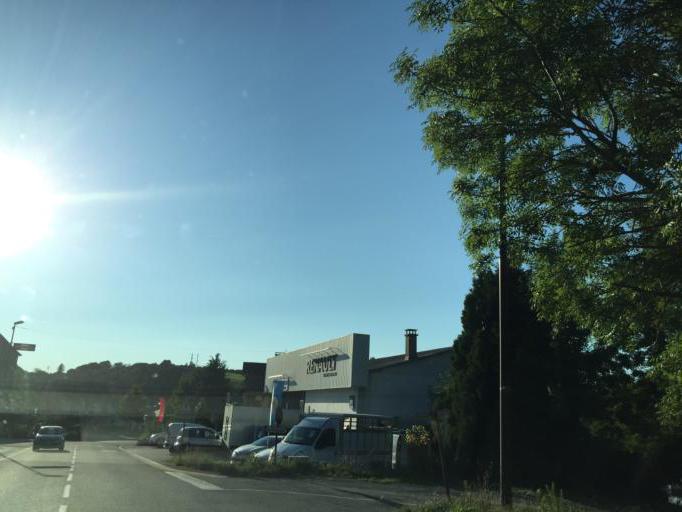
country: FR
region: Midi-Pyrenees
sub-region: Departement de l'Aveyron
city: Salles-Curan
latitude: 44.1804
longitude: 2.7920
